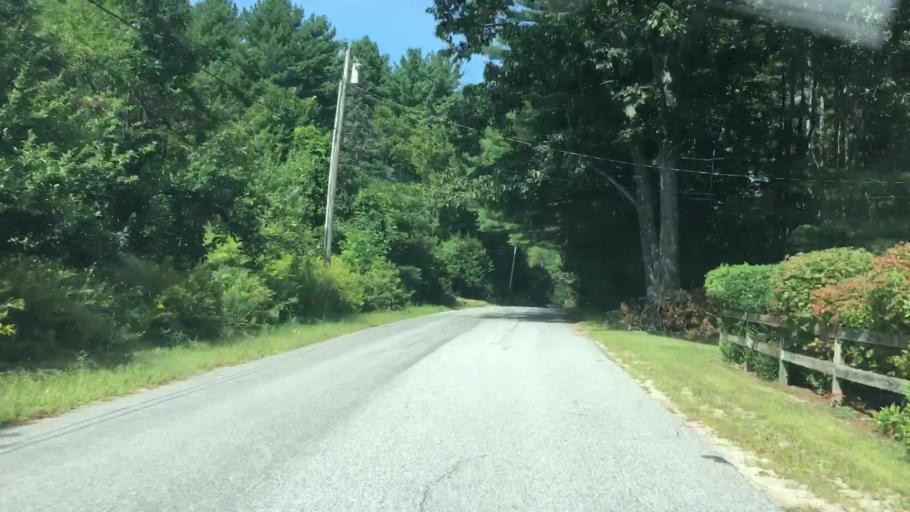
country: US
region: Maine
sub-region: Kennebec County
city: Monmouth
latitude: 44.2733
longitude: -70.0324
